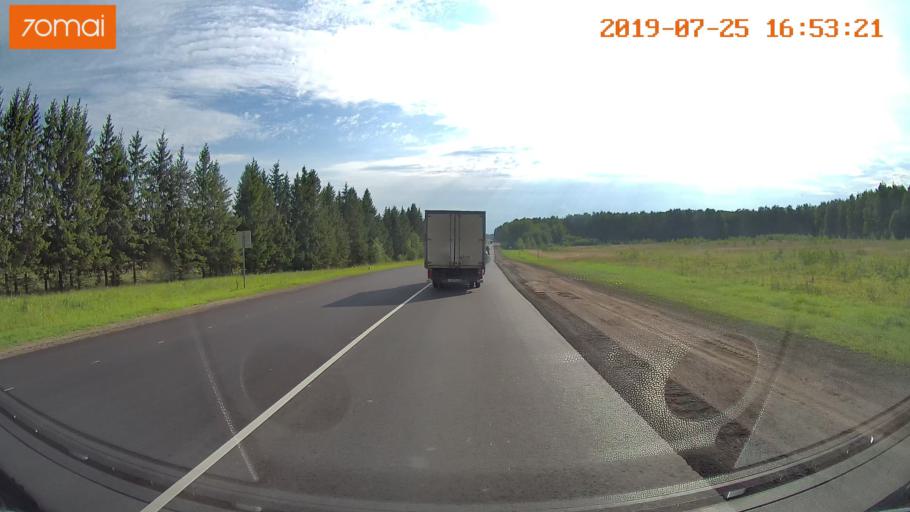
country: RU
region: Ivanovo
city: Furmanov
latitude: 57.3055
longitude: 41.2083
